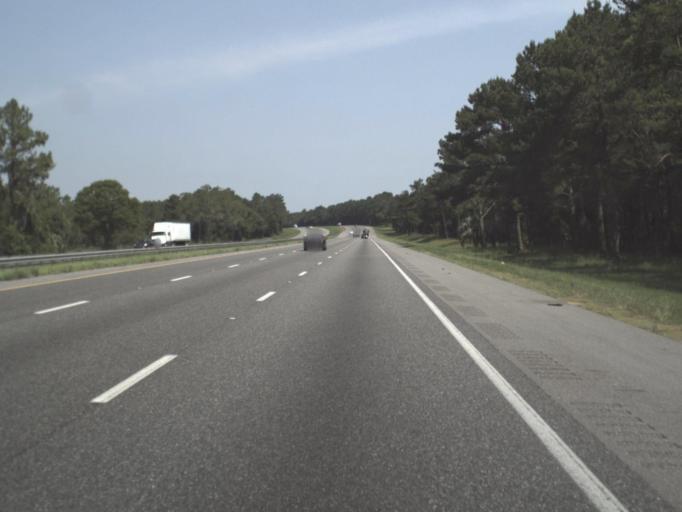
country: US
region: Florida
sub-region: Suwannee County
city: Wellborn
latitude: 30.3506
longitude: -82.8359
